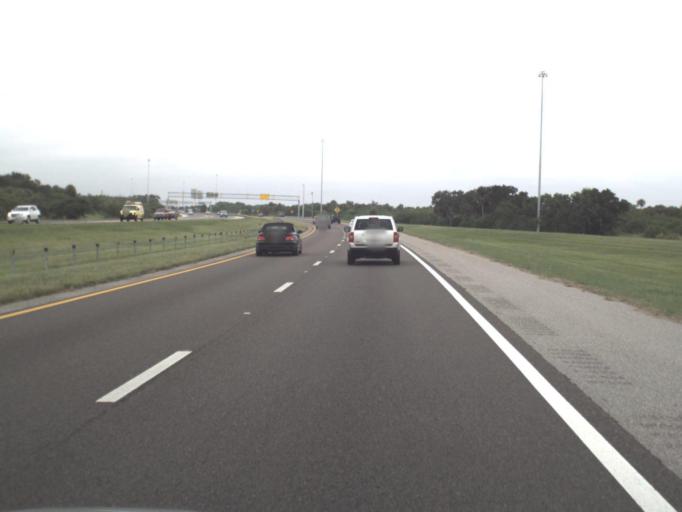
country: US
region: Florida
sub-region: Manatee County
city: Memphis
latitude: 27.5833
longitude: -82.5837
